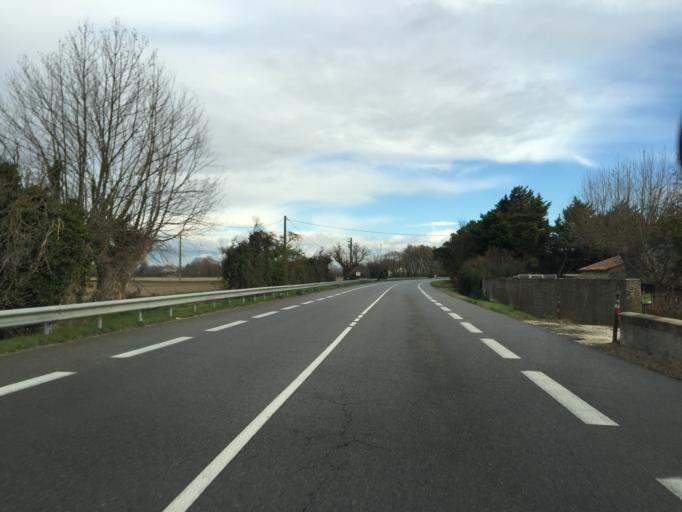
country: FR
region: Provence-Alpes-Cote d'Azur
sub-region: Departement du Vaucluse
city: Velleron
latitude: 43.9794
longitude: 5.0029
